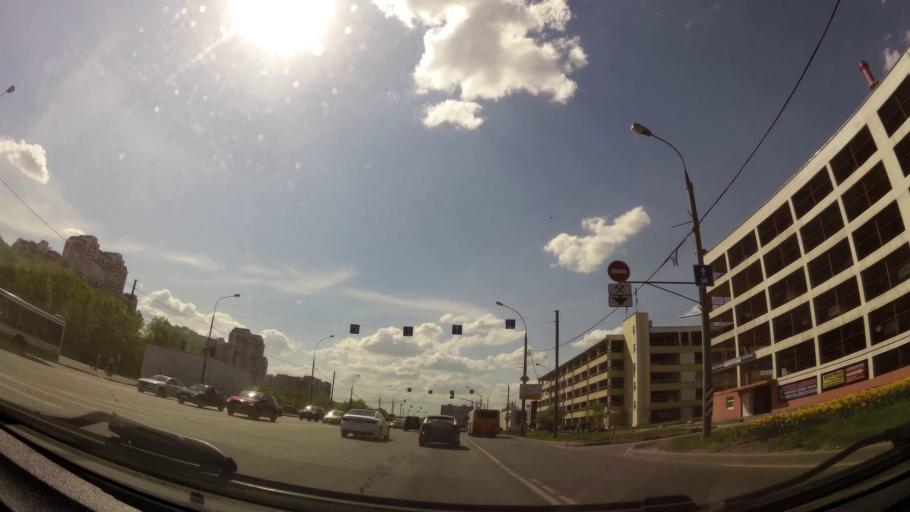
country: RU
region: Moskovskaya
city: Zarech'ye
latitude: 55.6594
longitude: 37.4059
